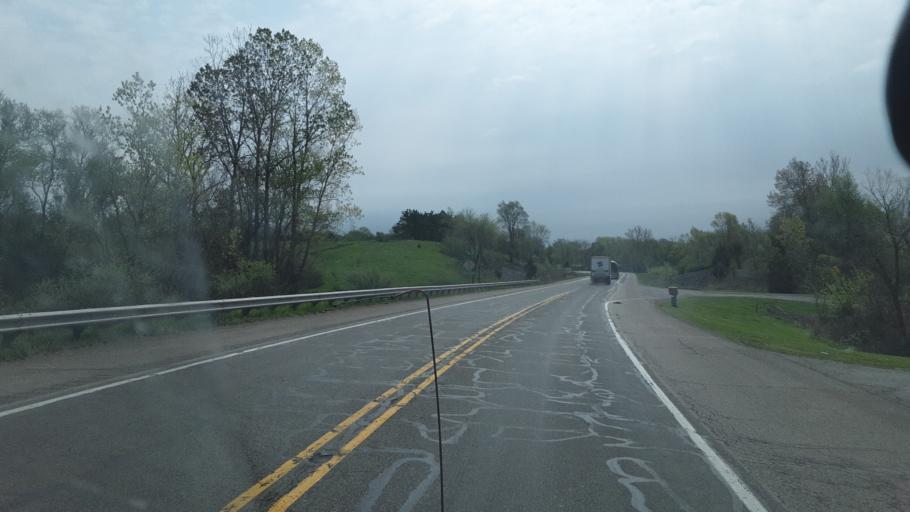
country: US
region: Indiana
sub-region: Steuben County
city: Angola
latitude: 41.6358
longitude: -85.0669
